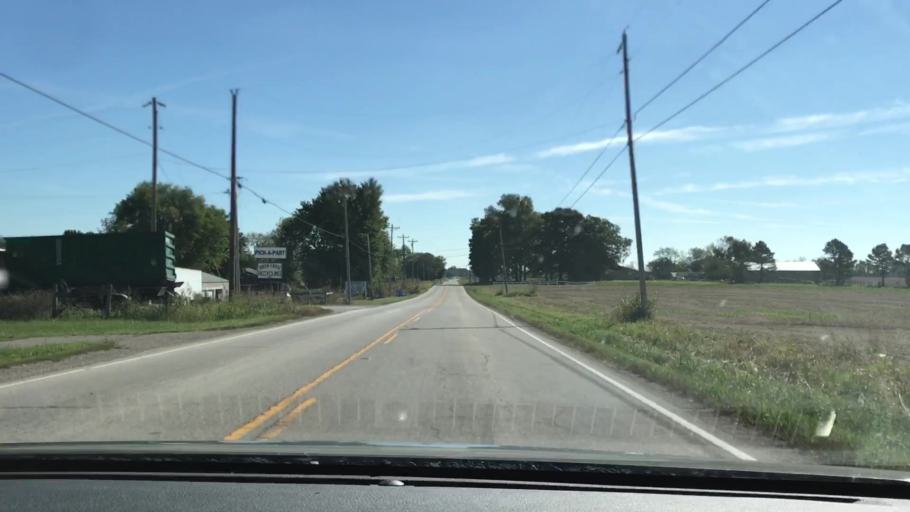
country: US
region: Kentucky
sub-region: Christian County
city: Hopkinsville
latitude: 36.8625
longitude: -87.4426
